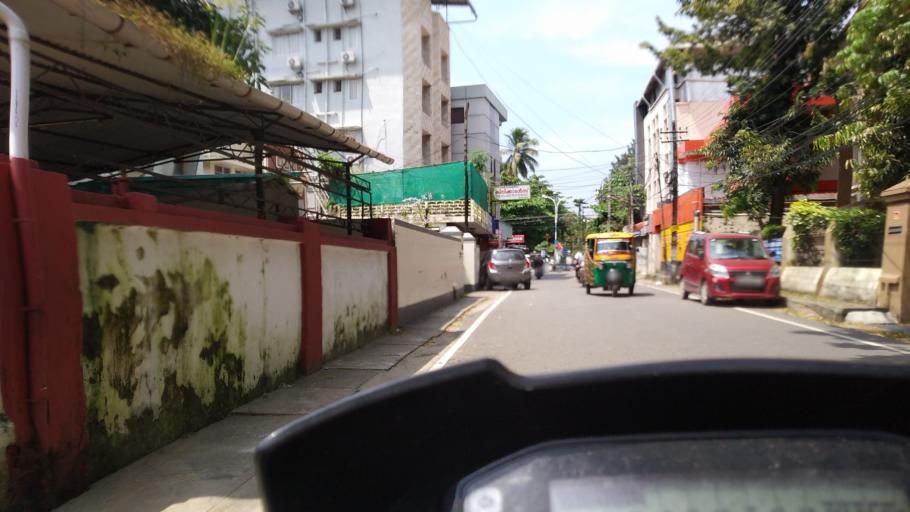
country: IN
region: Kerala
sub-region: Ernakulam
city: Cochin
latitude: 9.9673
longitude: 76.2836
